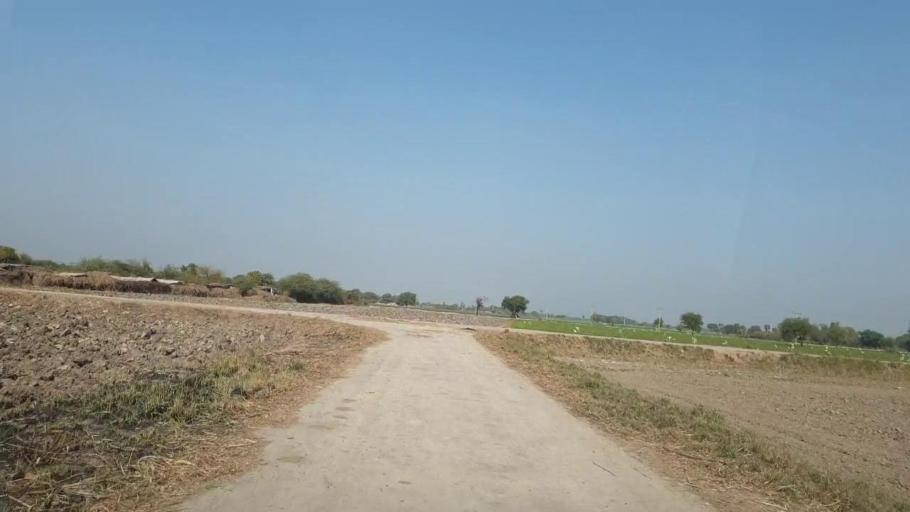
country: PK
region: Sindh
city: Matiari
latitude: 25.5051
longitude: 68.4712
